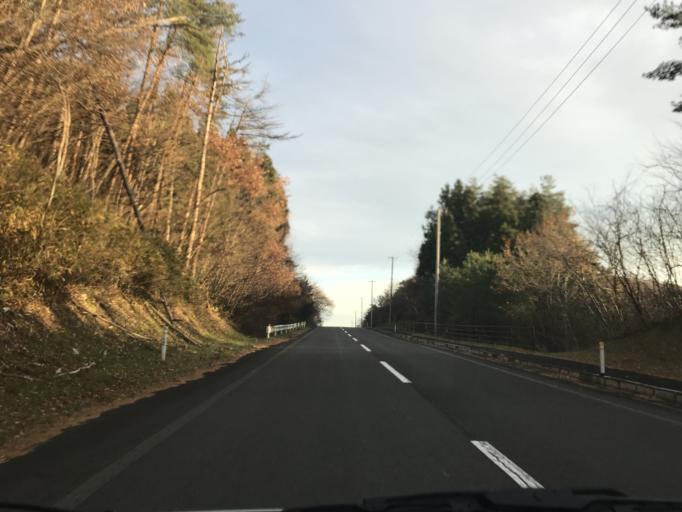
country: JP
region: Iwate
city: Ichinoseki
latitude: 38.9830
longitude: 141.0682
